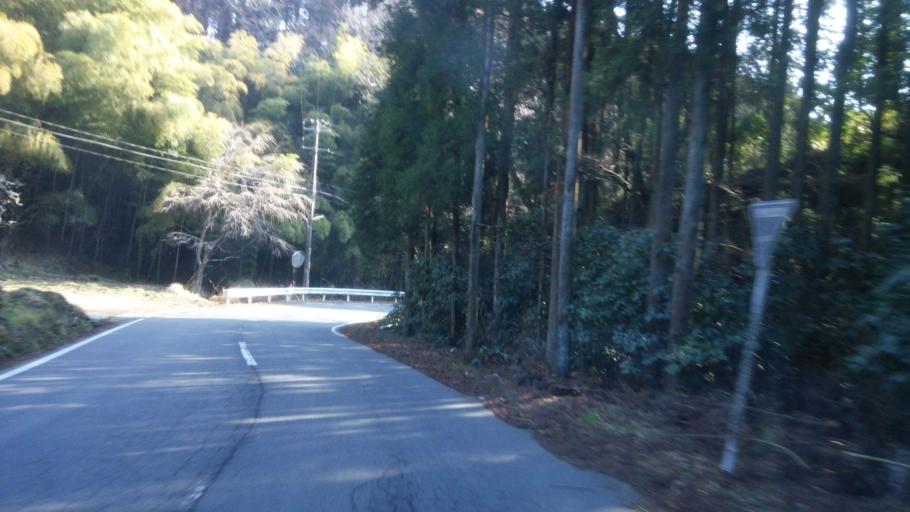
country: JP
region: Fukushima
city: Iwaki
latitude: 37.0256
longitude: 140.8191
